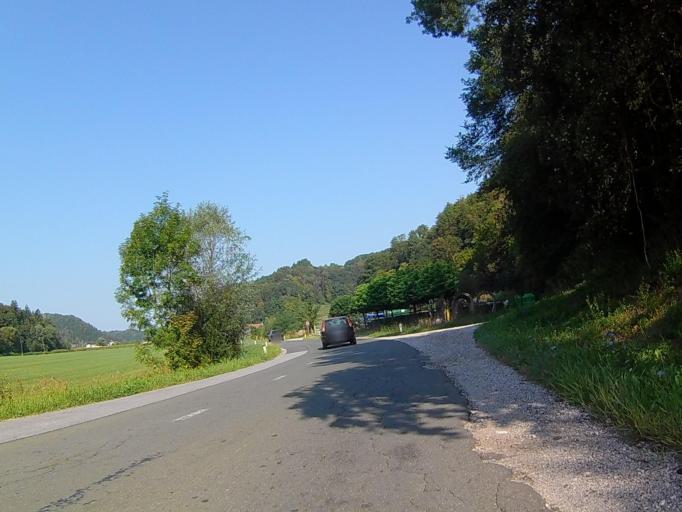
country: SI
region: Kungota
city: Zgornja Kungota
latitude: 46.6380
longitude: 15.6084
